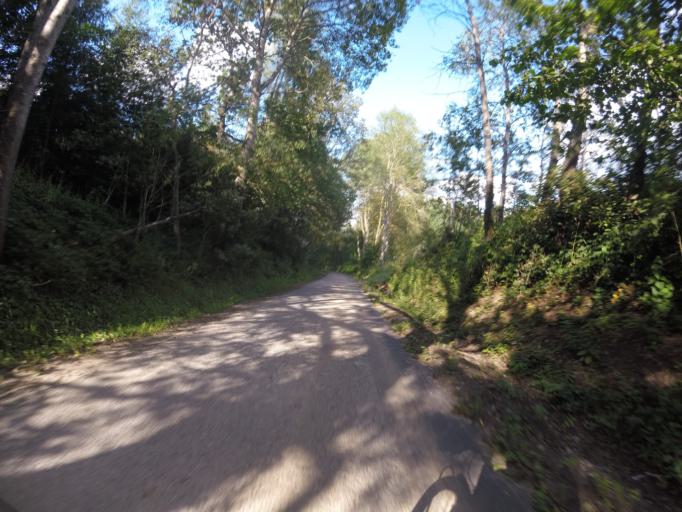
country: DE
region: Baden-Wuerttemberg
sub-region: Regierungsbezirk Stuttgart
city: Fichtenberg
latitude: 48.9440
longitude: 9.7021
